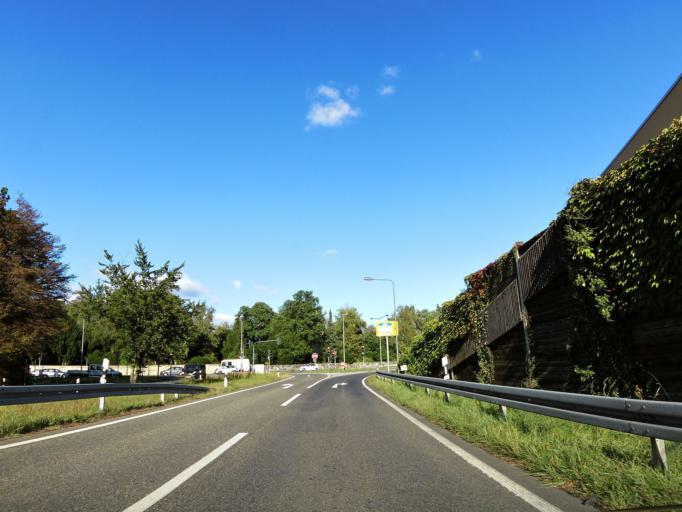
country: DE
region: Hesse
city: Kelsterbach
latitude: 50.0894
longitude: 8.5728
